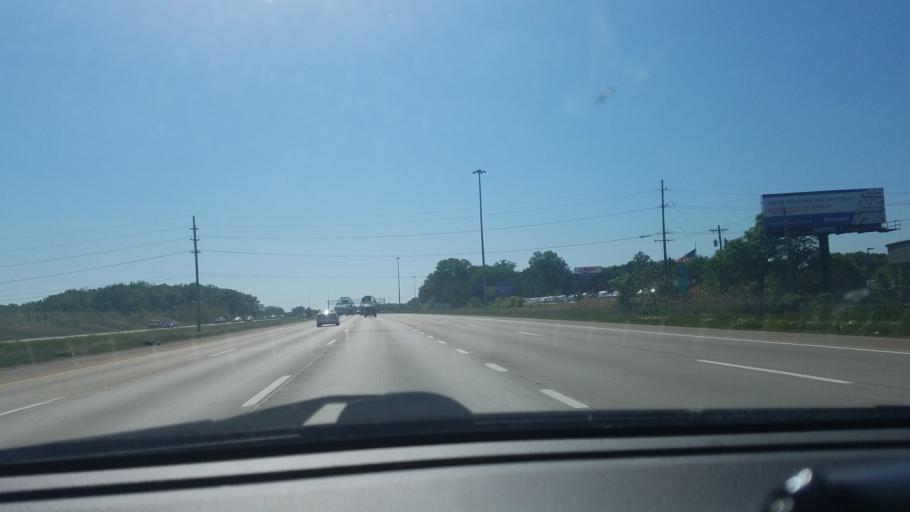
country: US
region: Michigan
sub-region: Wayne County
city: Taylor
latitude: 42.2669
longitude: -83.2578
